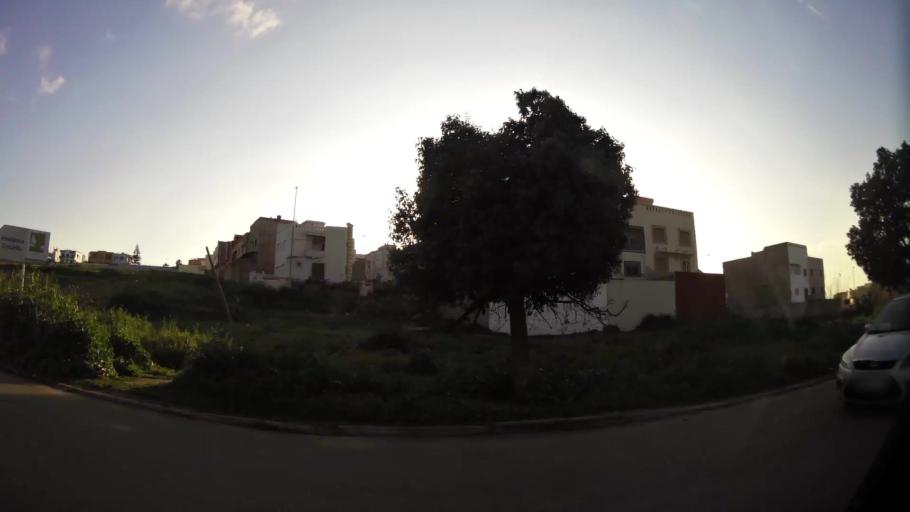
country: MA
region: Chaouia-Ouardigha
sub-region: Settat Province
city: Settat
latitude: 33.0089
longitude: -7.6106
